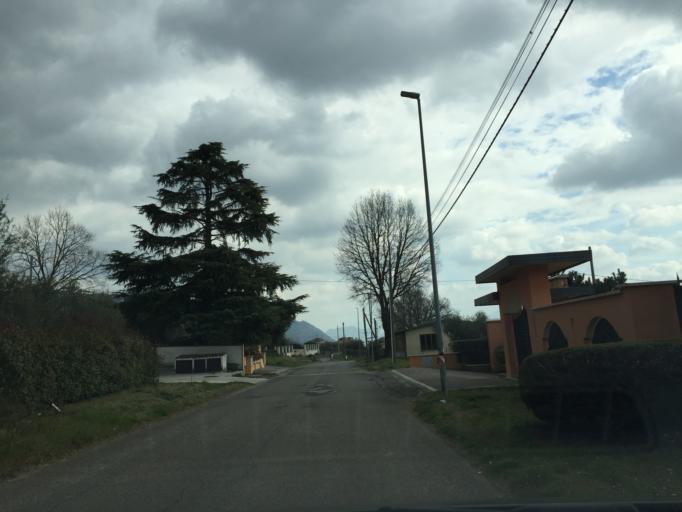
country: IT
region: Latium
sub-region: Provincia di Frosinone
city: Piedimonte San Germano Alta
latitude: 41.5004
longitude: 13.7403
